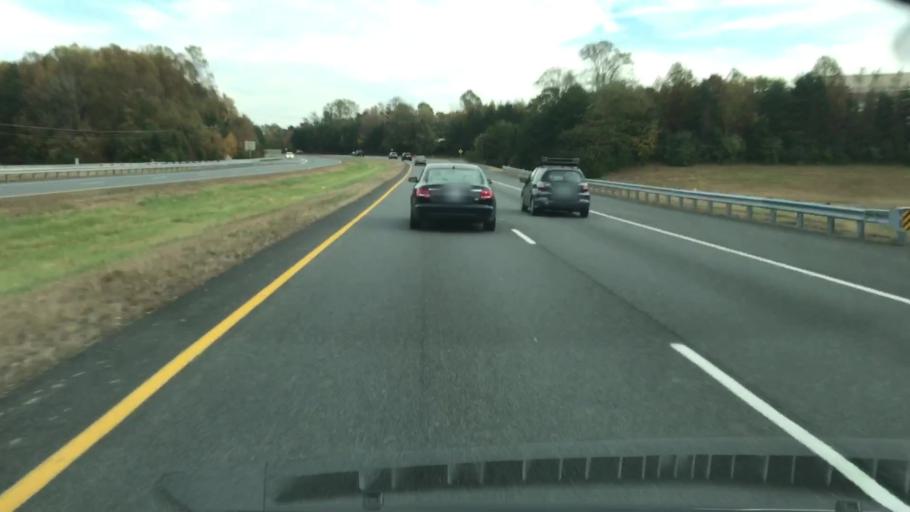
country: US
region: Virginia
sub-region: Fairfax County
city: Fairfax Station
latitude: 38.7879
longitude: -77.3257
